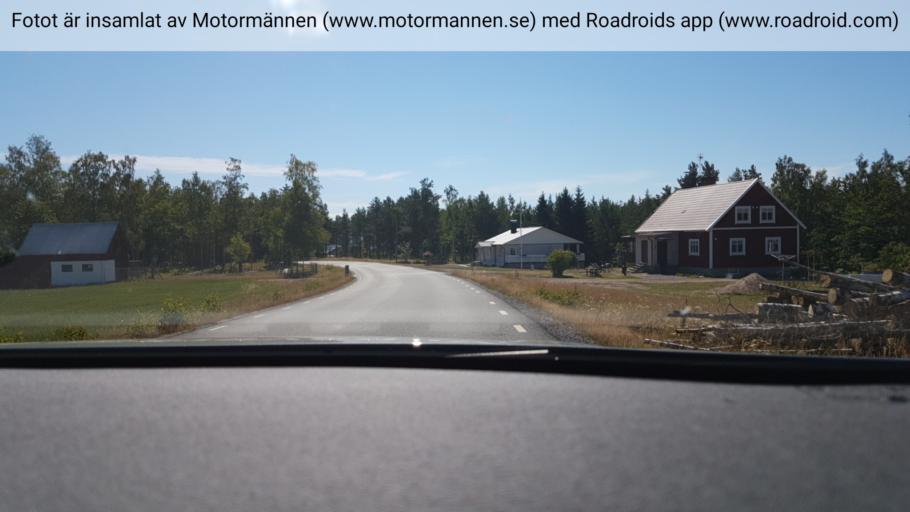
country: SE
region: Joenkoeping
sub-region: Habo Kommun
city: Habo
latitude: 58.0981
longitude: 14.1965
